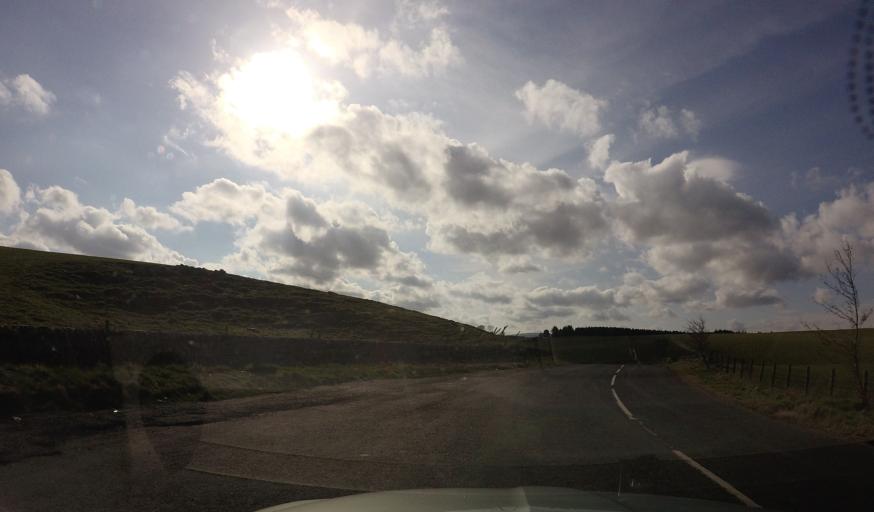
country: GB
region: Scotland
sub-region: Midlothian
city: Penicuik
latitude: 55.8111
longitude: -3.1853
